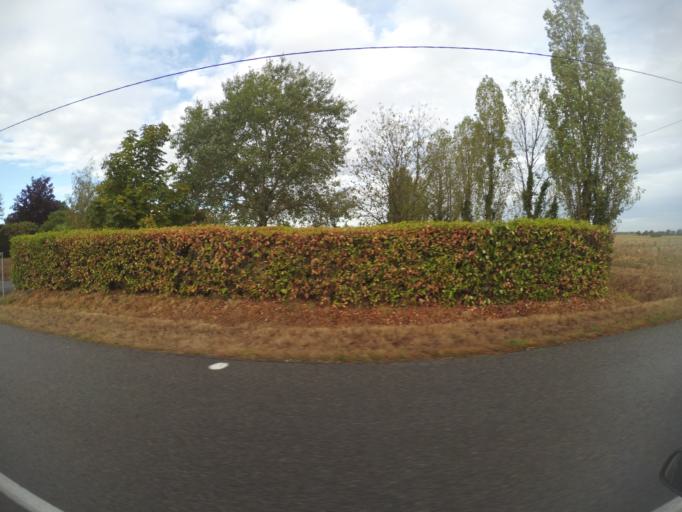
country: FR
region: Pays de la Loire
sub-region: Departement de la Loire-Atlantique
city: La Planche
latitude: 47.0440
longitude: -1.4149
